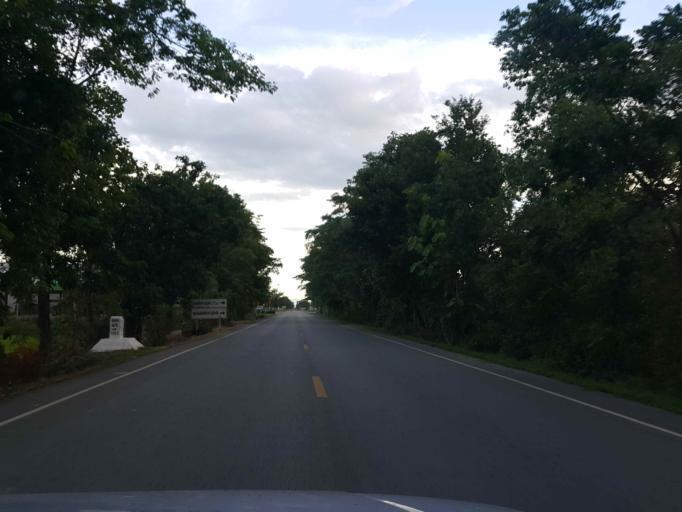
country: TH
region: Sukhothai
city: Sawankhalok
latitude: 17.3117
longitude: 99.7335
